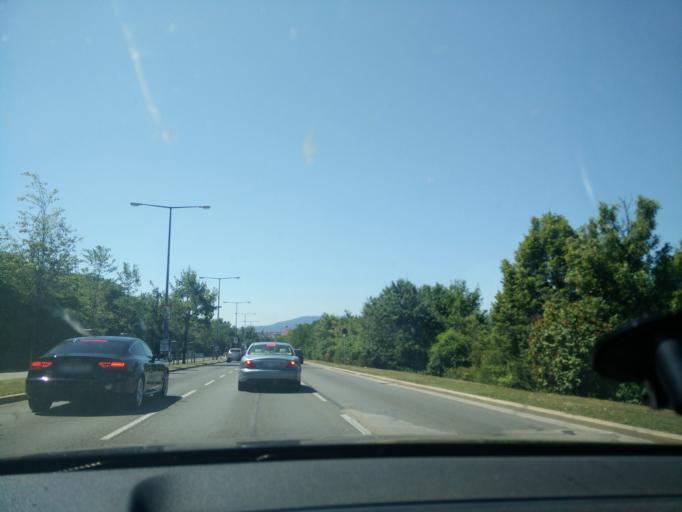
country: AT
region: Lower Austria
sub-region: Politischer Bezirk Modling
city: Vosendorf
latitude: 48.1609
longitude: 16.3443
